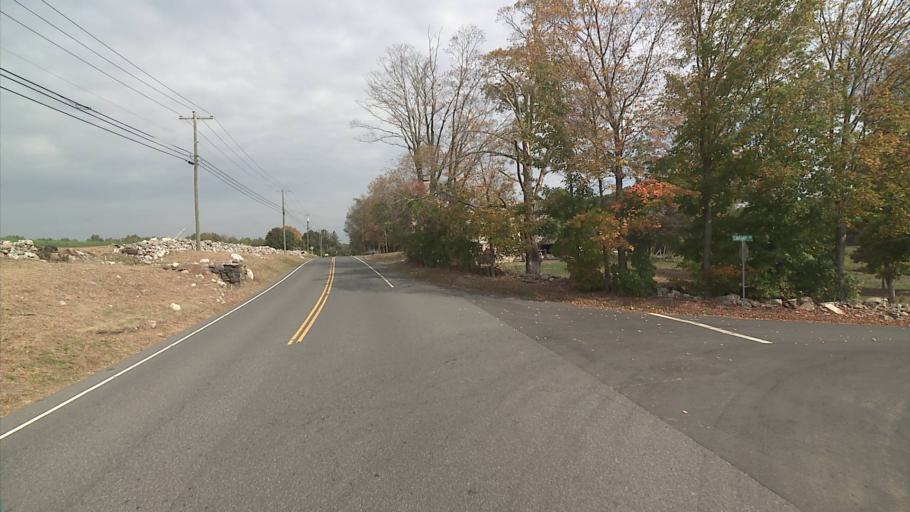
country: US
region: Connecticut
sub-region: Litchfield County
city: Watertown
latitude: 41.5906
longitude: -73.1708
